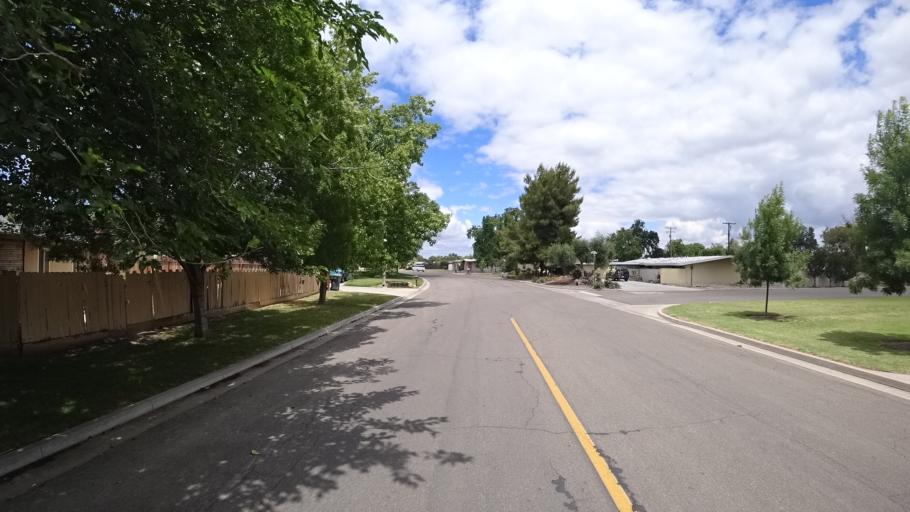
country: US
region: California
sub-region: Kings County
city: Hanford
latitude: 36.3482
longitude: -119.6511
